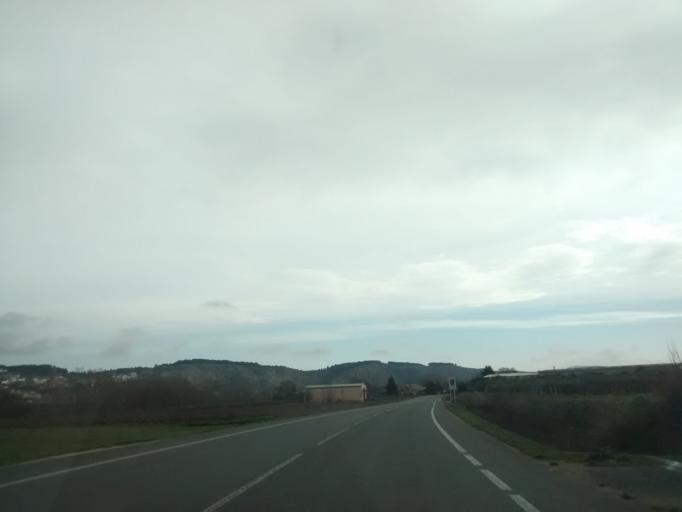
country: ES
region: Navarre
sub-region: Provincia de Navarra
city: Andosilla
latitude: 42.3779
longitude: -1.9554
